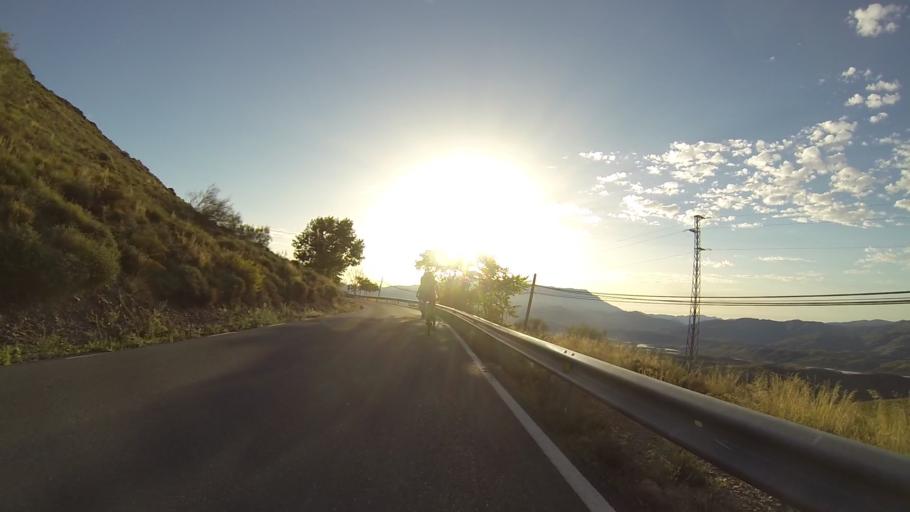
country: ES
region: Andalusia
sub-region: Provincia de Granada
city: Valor
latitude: 36.9782
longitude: -3.1261
